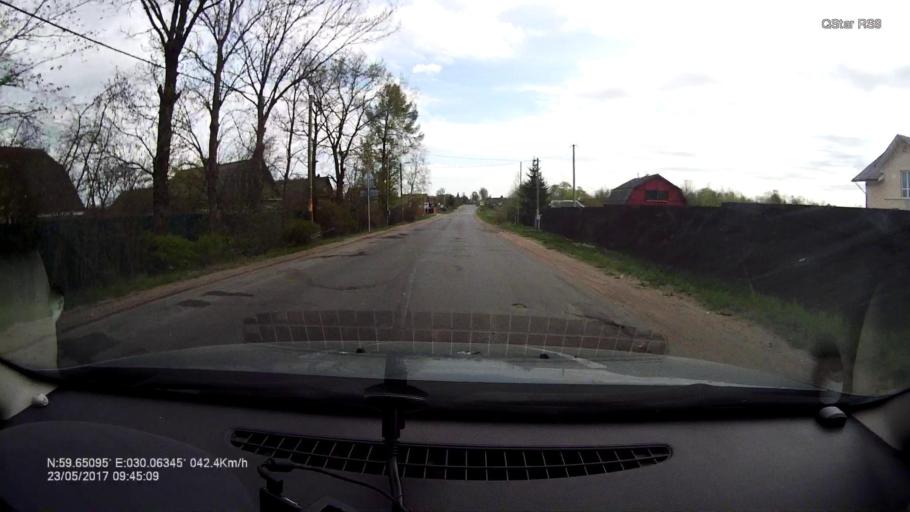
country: RU
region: Leningrad
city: Taytsy
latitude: 59.6510
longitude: 30.0635
